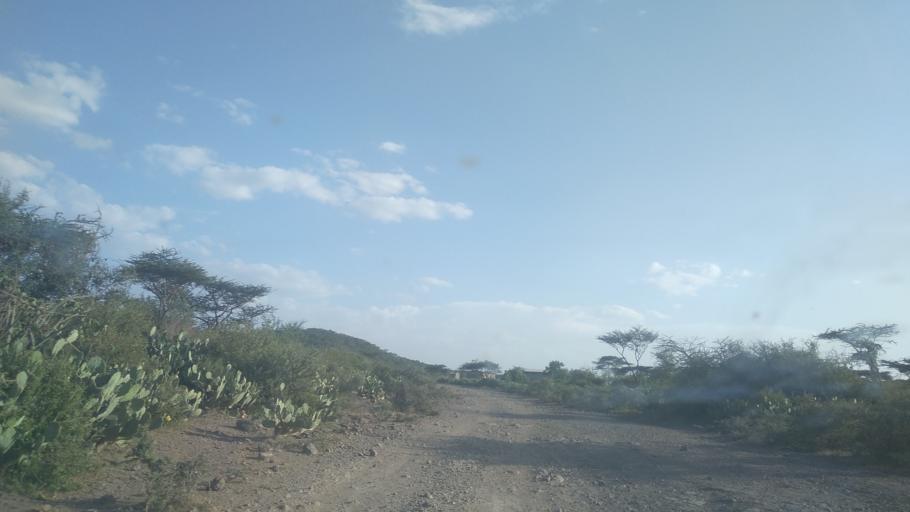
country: ET
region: Oromiya
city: Hirna
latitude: 9.4003
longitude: 40.9482
